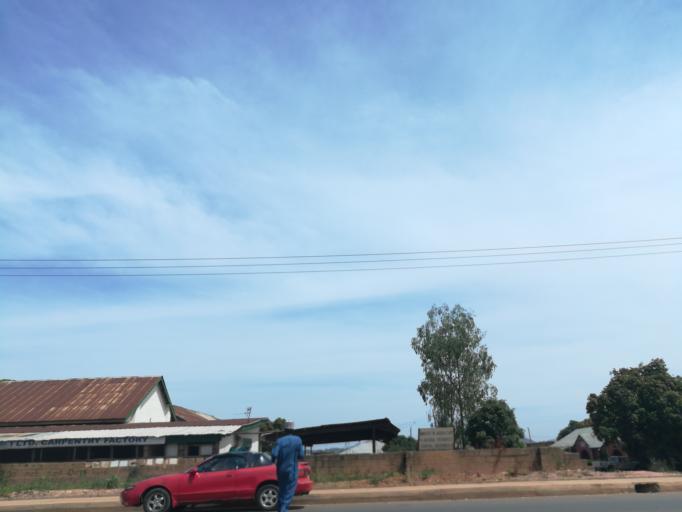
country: NG
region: Plateau
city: Bukuru
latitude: 9.7759
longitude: 8.8605
